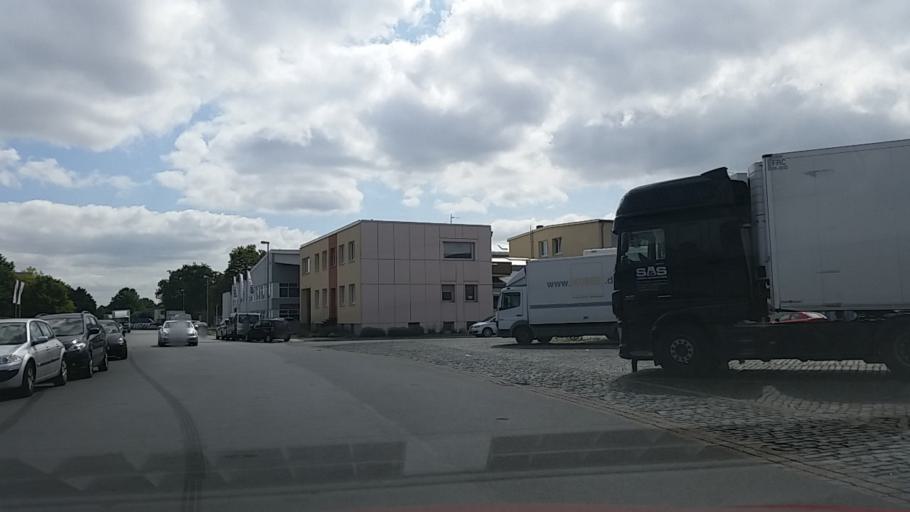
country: DE
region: Lower Saxony
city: Langenhagen
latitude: 52.4200
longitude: 9.7396
